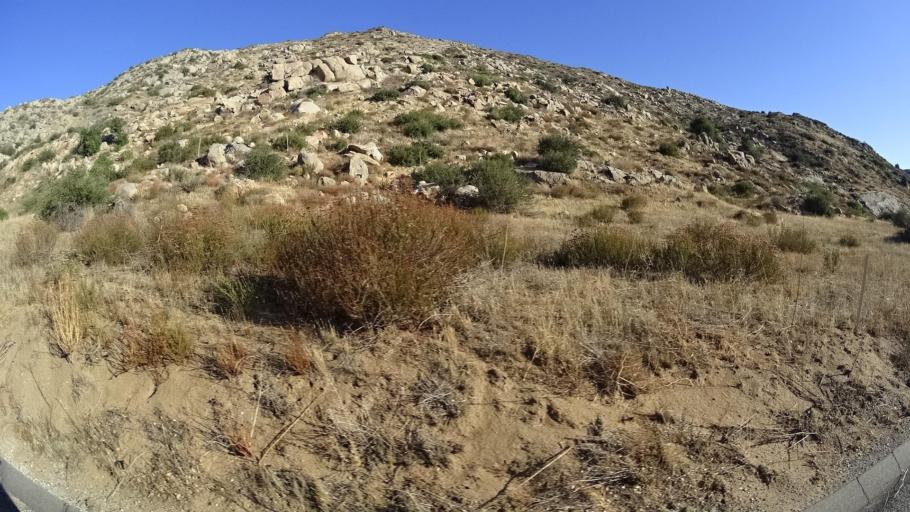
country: MX
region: Baja California
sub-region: Tecate
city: Hacienda Tecate
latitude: 32.5958
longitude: -116.5375
